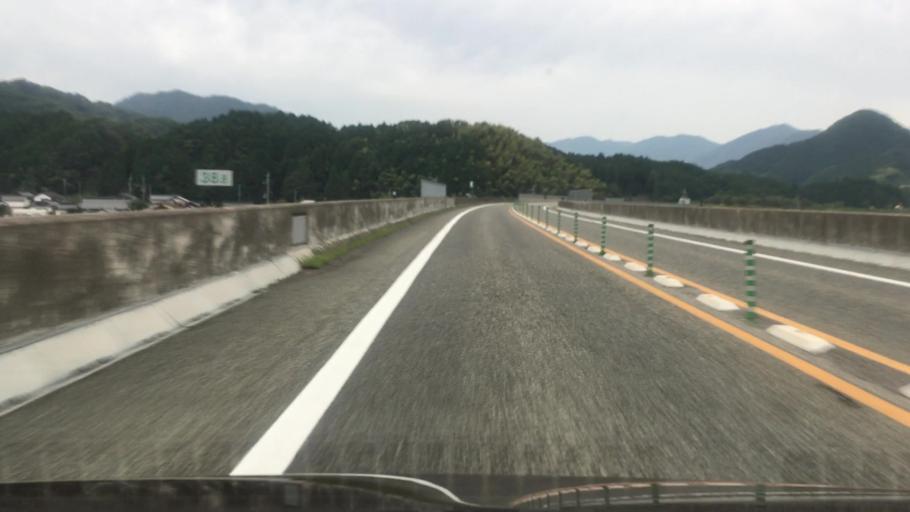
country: JP
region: Kyoto
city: Fukuchiyama
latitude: 35.3055
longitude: 134.8838
